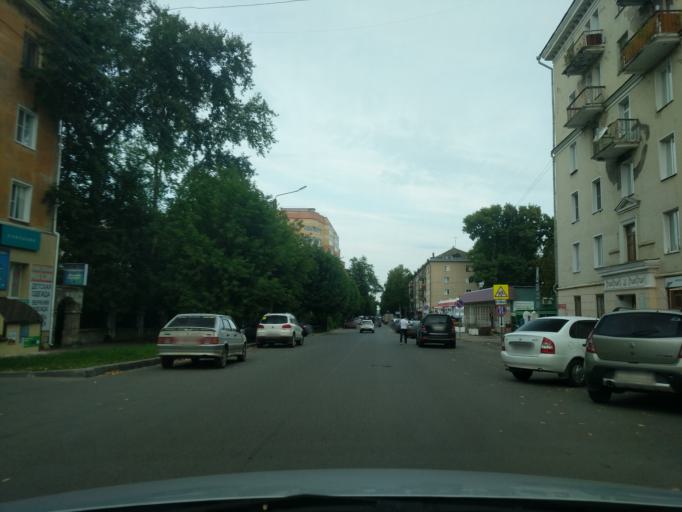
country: RU
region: Kirov
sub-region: Kirovo-Chepetskiy Rayon
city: Kirov
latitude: 58.6113
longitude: 49.6574
